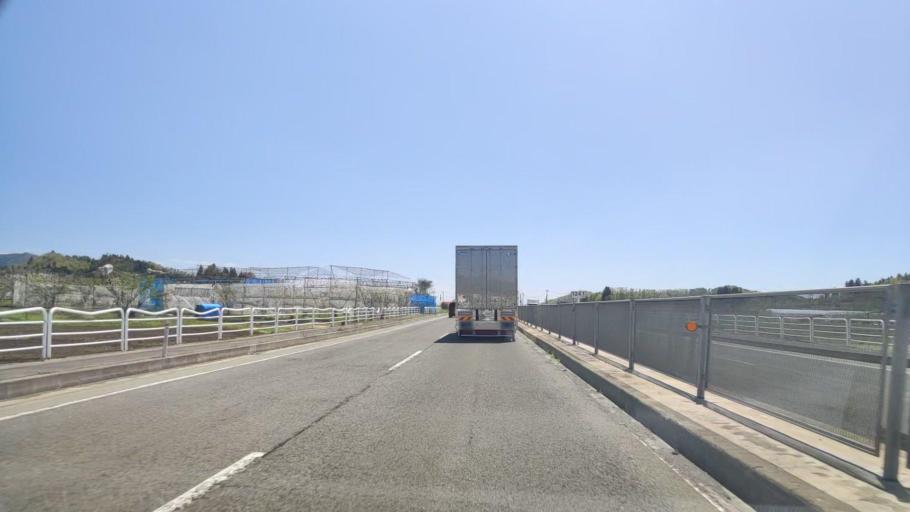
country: JP
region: Yamagata
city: Obanazawa
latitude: 38.5407
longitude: 140.3951
